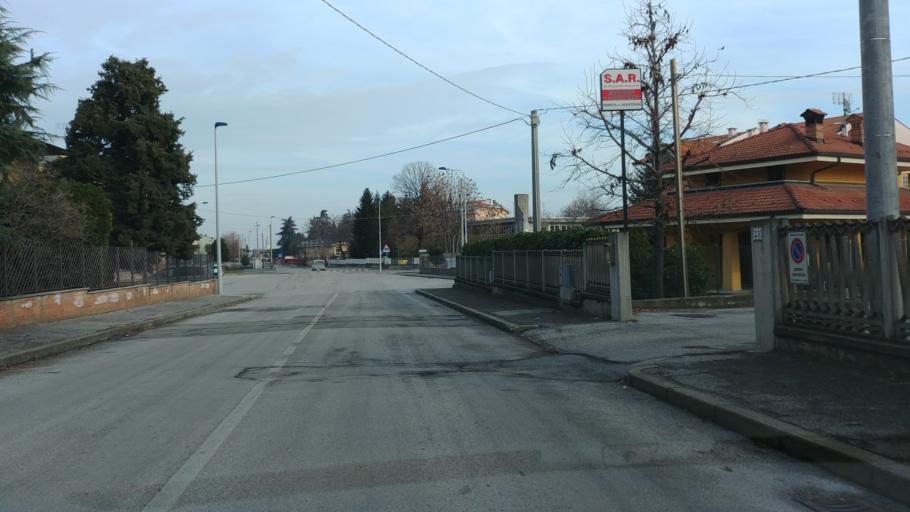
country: IT
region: Piedmont
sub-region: Provincia di Cuneo
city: Cuneo
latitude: 44.3879
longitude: 7.5652
